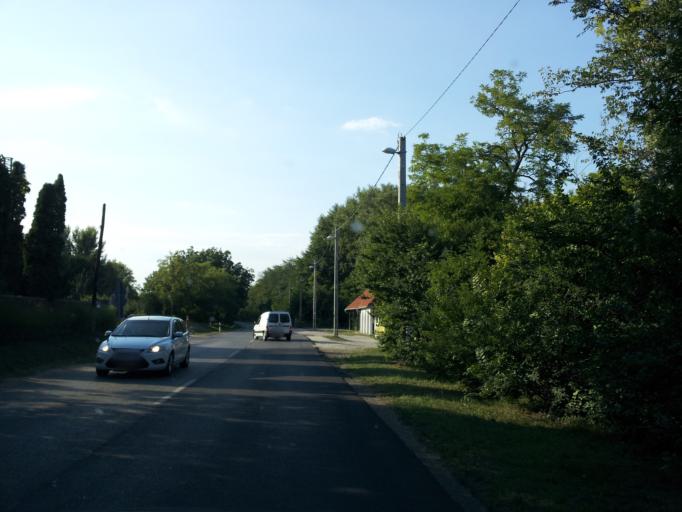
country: HU
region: Pest
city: Tahitotfalu
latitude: 47.7608
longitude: 19.0706
